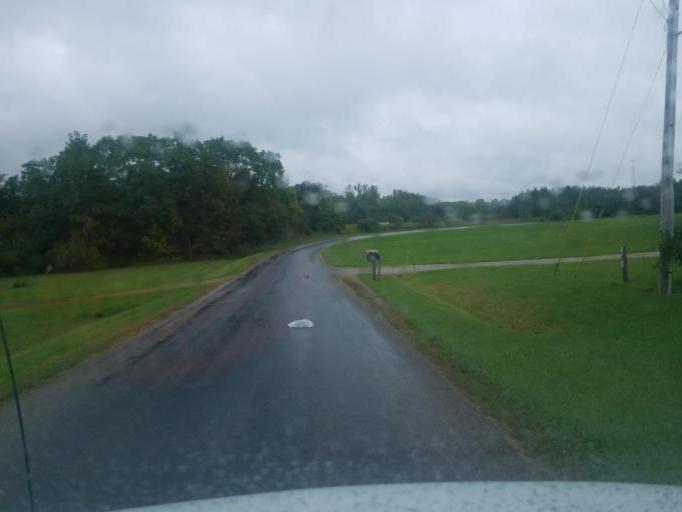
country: US
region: Ohio
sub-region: Wayne County
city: West Salem
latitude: 40.9283
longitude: -82.1188
